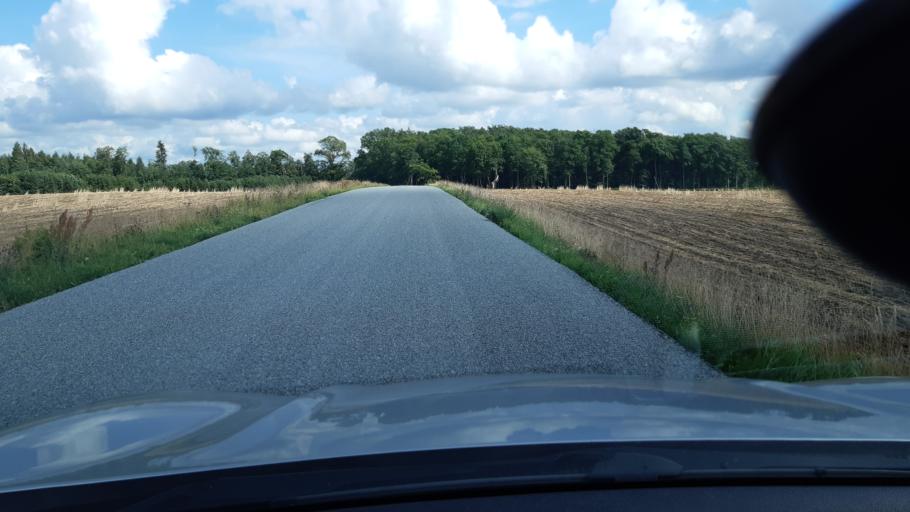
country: EE
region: Raplamaa
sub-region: Kehtna vald
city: Kehtna
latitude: 58.9036
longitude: 25.0900
